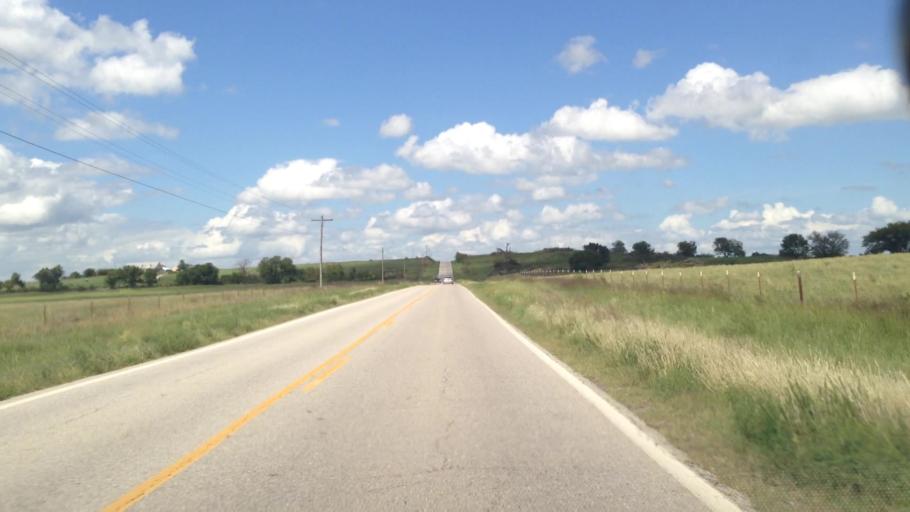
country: US
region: Oklahoma
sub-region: Craig County
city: Vinita
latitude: 36.7002
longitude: -95.1436
